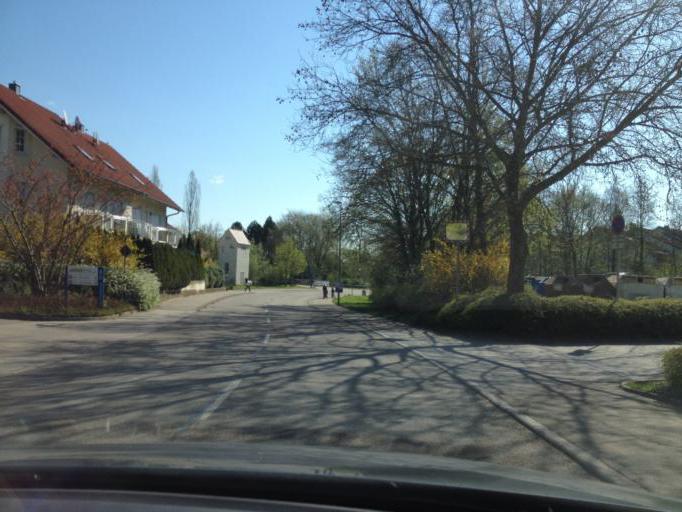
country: DE
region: Baden-Wuerttemberg
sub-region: Regierungsbezirk Stuttgart
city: Neuenstadt am Kocher
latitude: 49.2336
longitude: 9.3291
